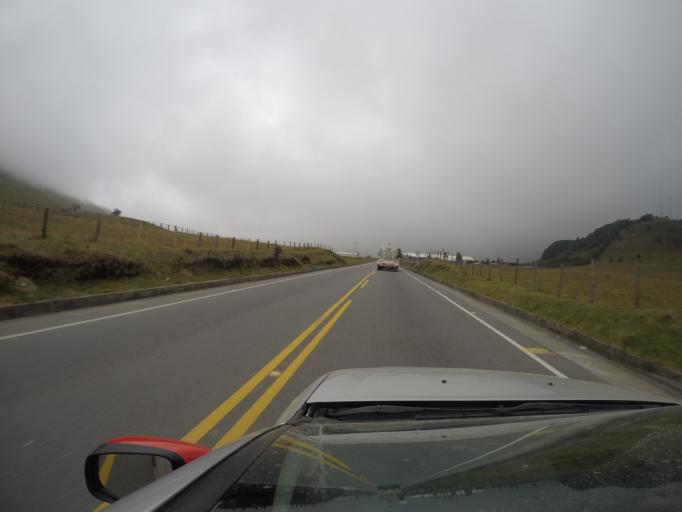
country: CO
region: Tolima
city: Herveo
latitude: 5.0424
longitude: -75.3341
